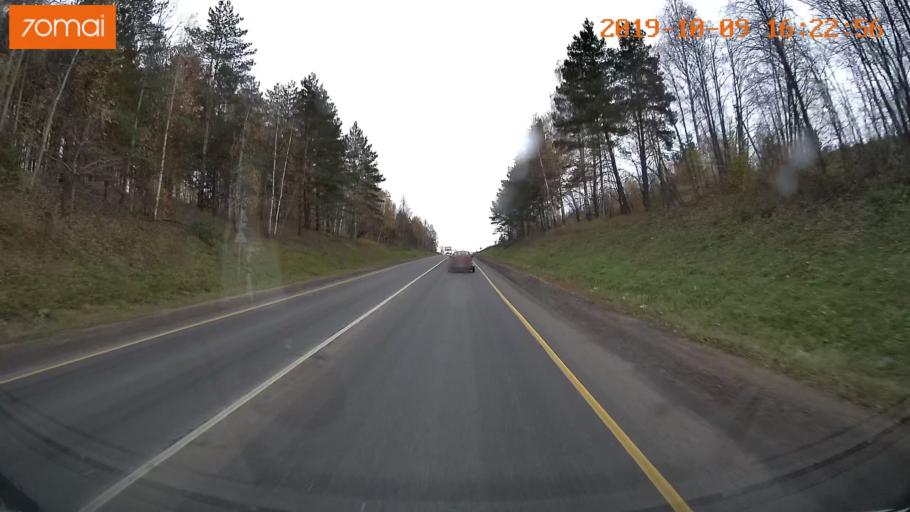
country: RU
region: Kostroma
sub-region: Kostromskoy Rayon
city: Kostroma
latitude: 57.6703
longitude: 40.8939
